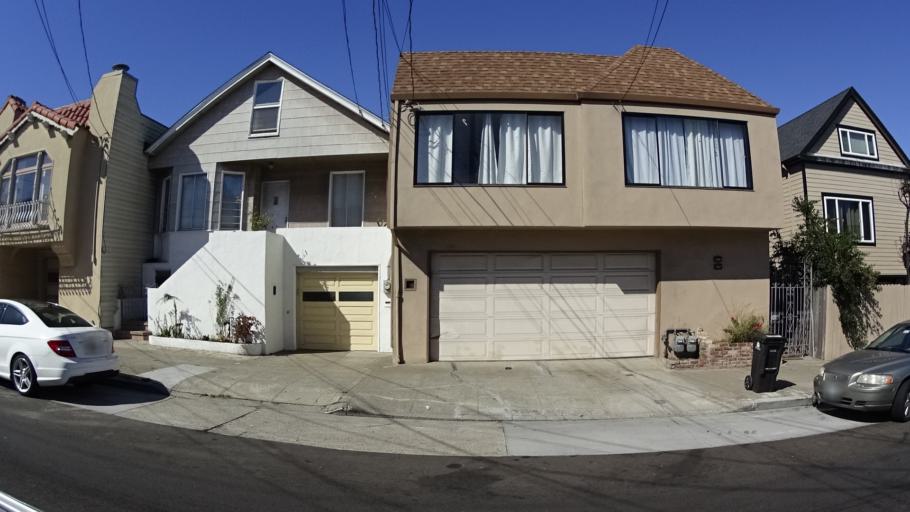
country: US
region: California
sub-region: San Francisco County
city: San Francisco
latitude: 37.7313
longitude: -122.4093
